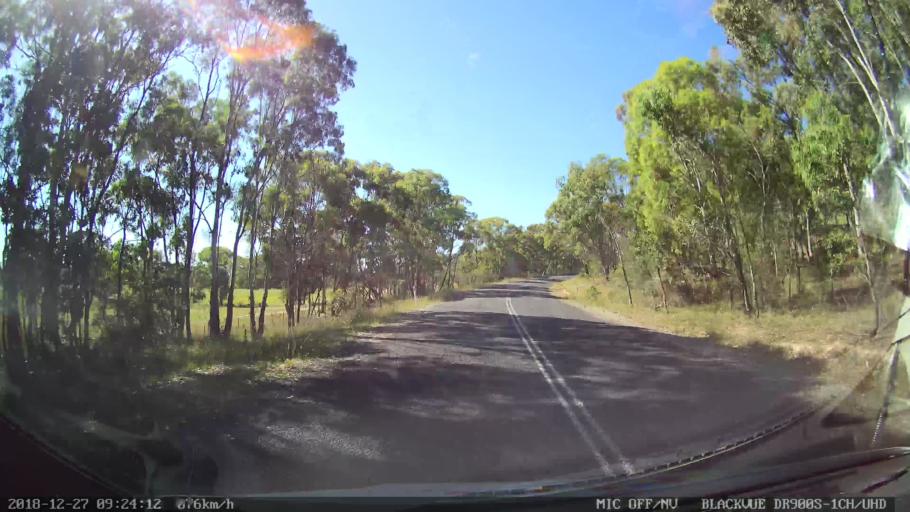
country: AU
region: New South Wales
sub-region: Lithgow
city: Portland
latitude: -33.1343
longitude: 149.9978
